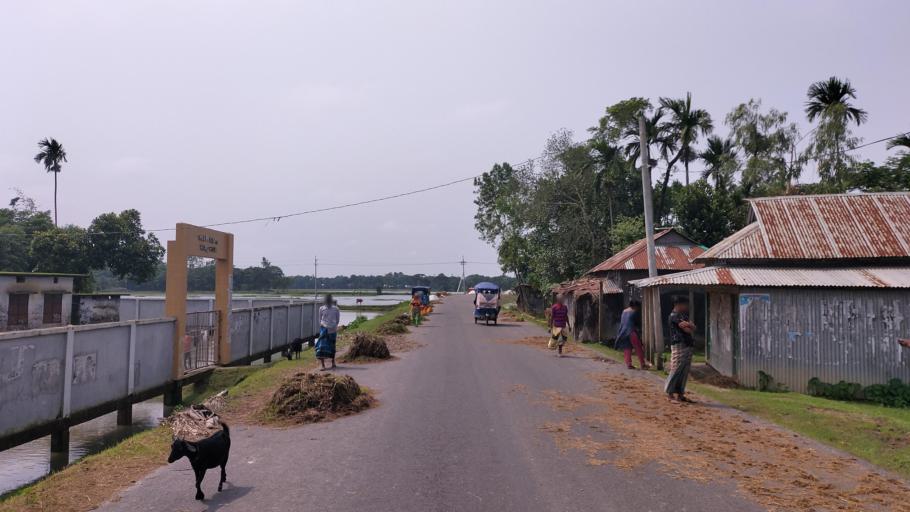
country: BD
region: Dhaka
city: Netrakona
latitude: 24.9597
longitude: 90.8343
